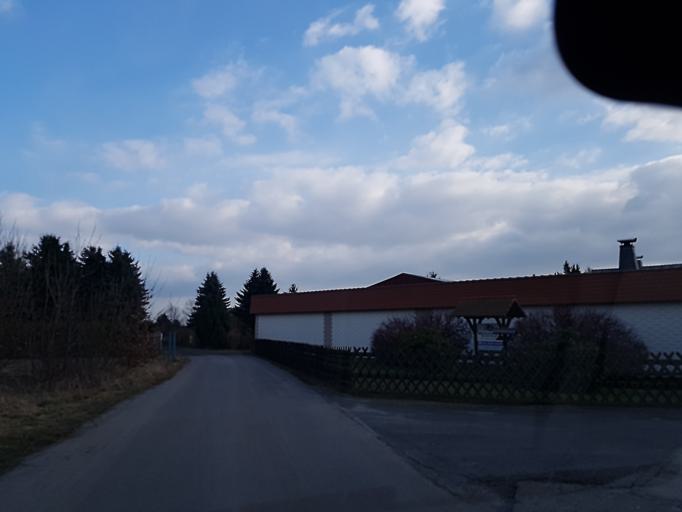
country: DE
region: Brandenburg
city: Finsterwalde
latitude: 51.6200
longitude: 13.7171
